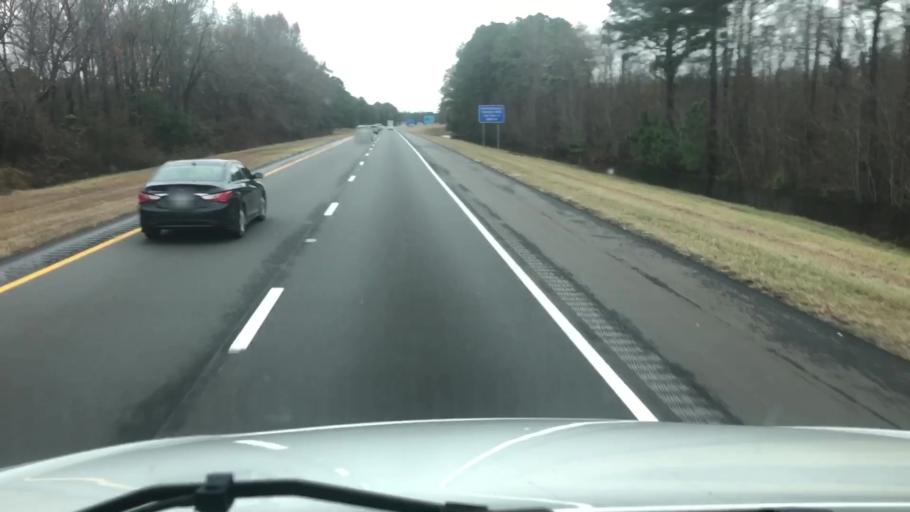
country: US
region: North Carolina
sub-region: Cumberland County
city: Eastover
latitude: 35.0690
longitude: -78.7920
